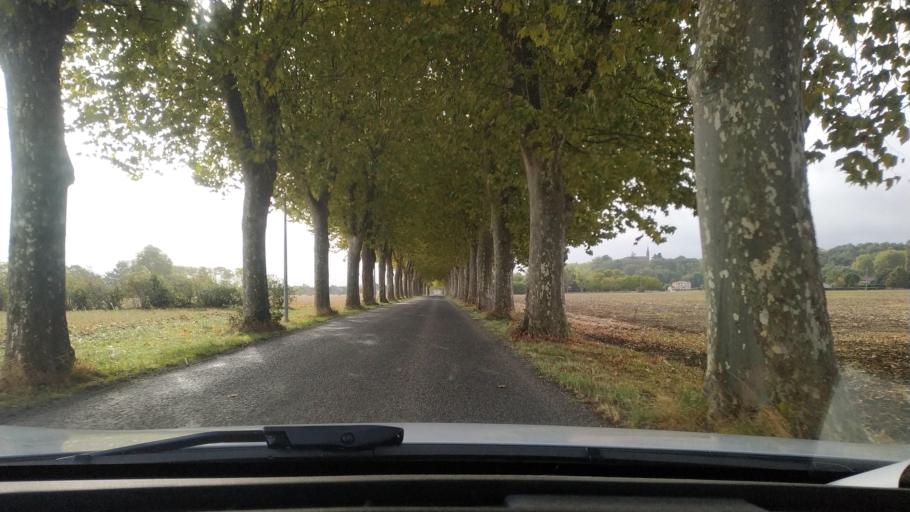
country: FR
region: Midi-Pyrenees
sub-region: Departement de la Haute-Garonne
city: Gaillac-Toulza
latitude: 43.2808
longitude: 1.4956
